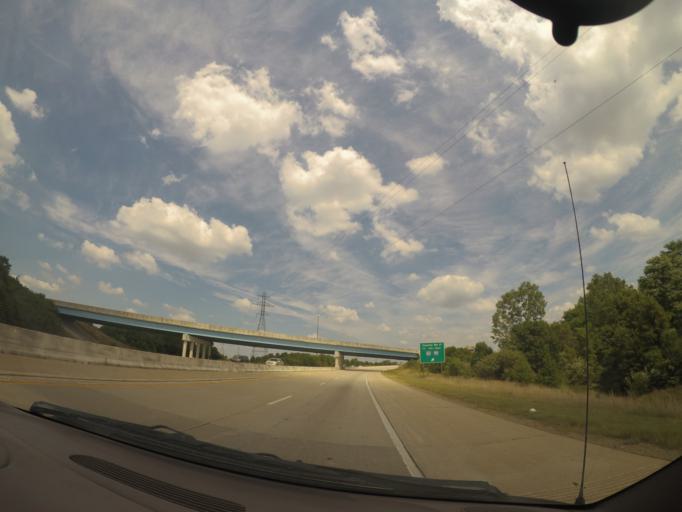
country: US
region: Indiana
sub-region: Elkhart County
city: Dunlap
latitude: 41.6658
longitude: -85.8956
